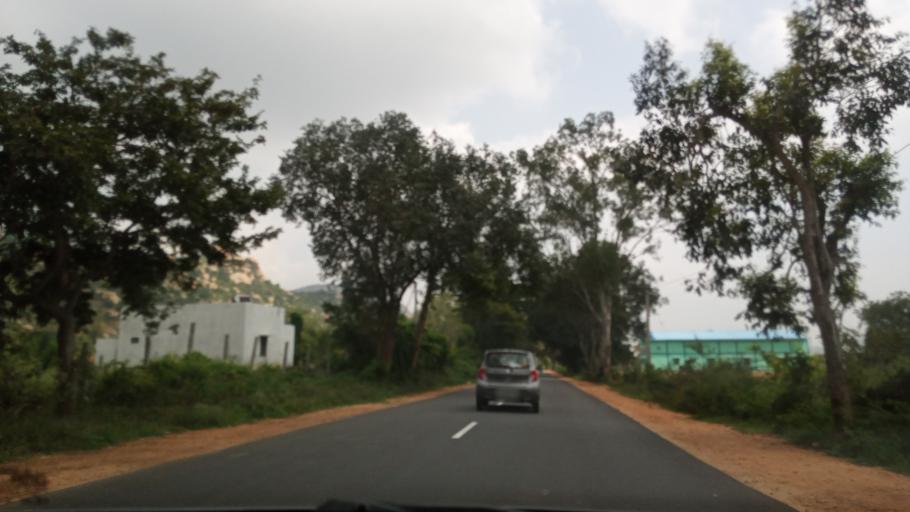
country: IN
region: Andhra Pradesh
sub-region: Chittoor
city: Madanapalle
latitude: 13.6366
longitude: 78.5900
